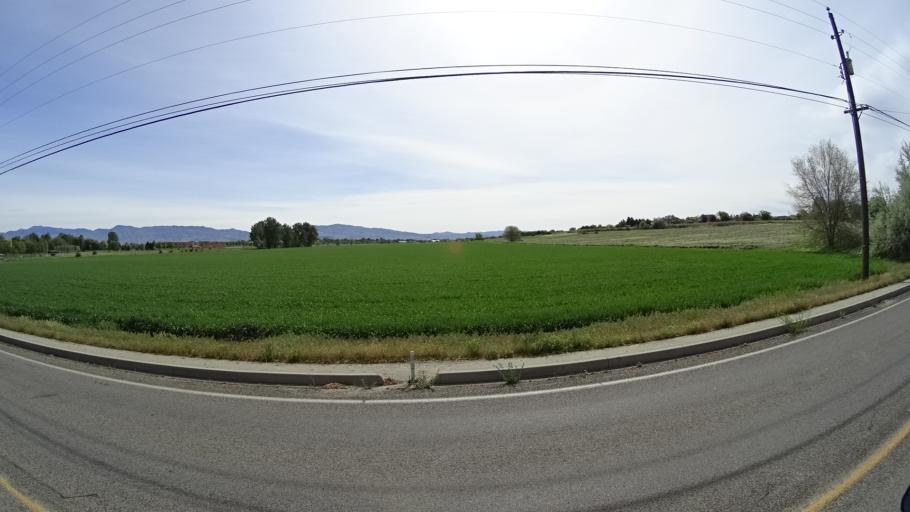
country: US
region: Idaho
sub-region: Ada County
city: Garden City
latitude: 43.5669
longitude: -116.2945
